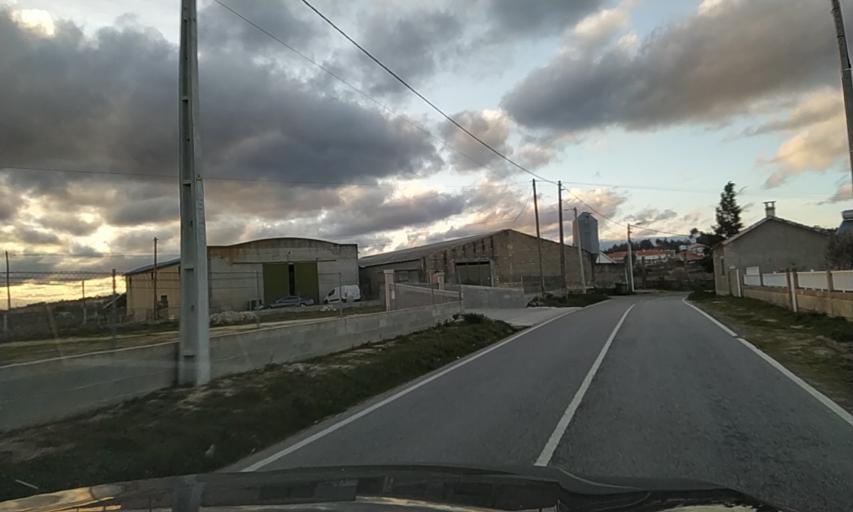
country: PT
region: Braganca
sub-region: Carrazeda de Ansiaes
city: Carrazeda de Anciaes
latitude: 41.2346
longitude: -7.3051
